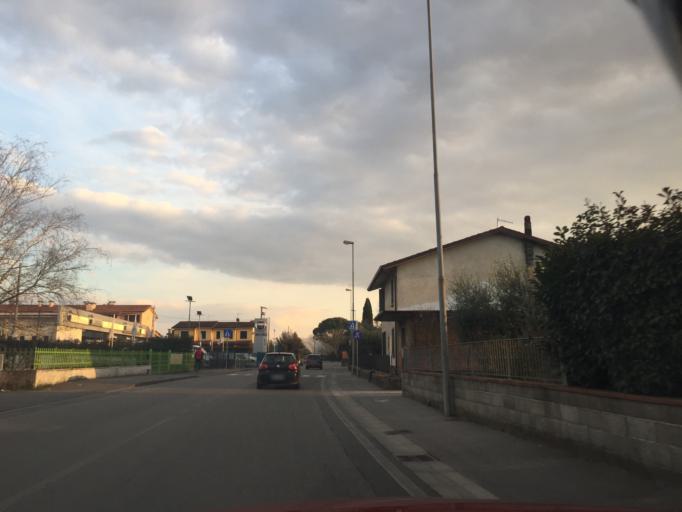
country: IT
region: Tuscany
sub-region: Provincia di Pistoia
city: Borgo a Buggiano
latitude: 43.8683
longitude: 10.7391
